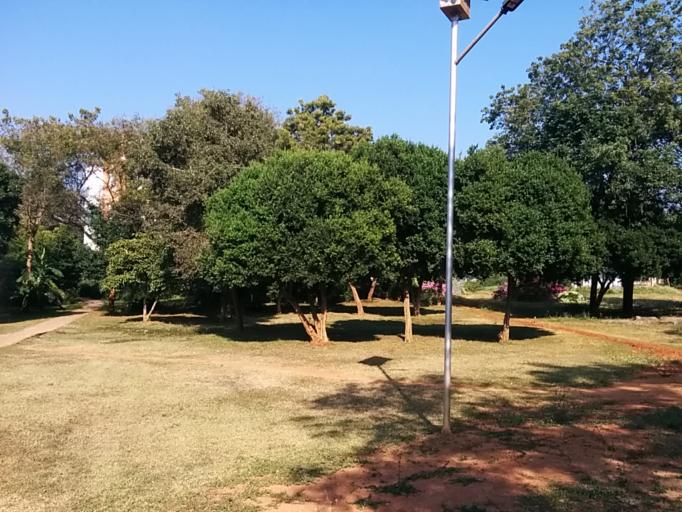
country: IN
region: Tamil Nadu
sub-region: Villupuram
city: Auroville
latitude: 12.0099
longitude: 79.8116
